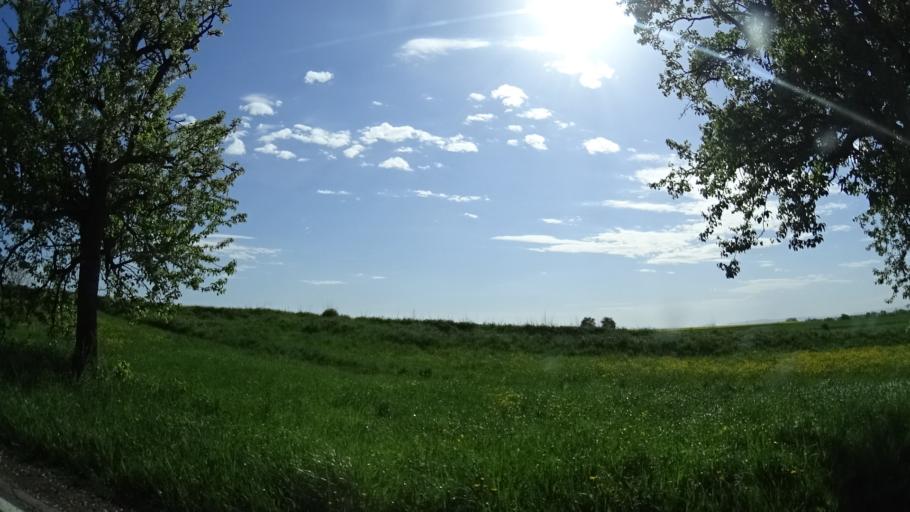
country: DE
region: Baden-Wuerttemberg
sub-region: Regierungsbezirk Stuttgart
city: Motzingen
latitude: 48.5004
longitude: 8.7740
